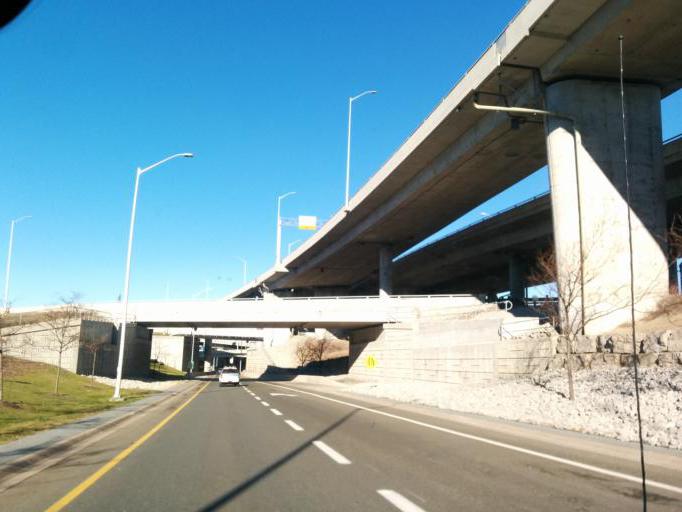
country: CA
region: Ontario
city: Etobicoke
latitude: 43.6844
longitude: -79.6109
